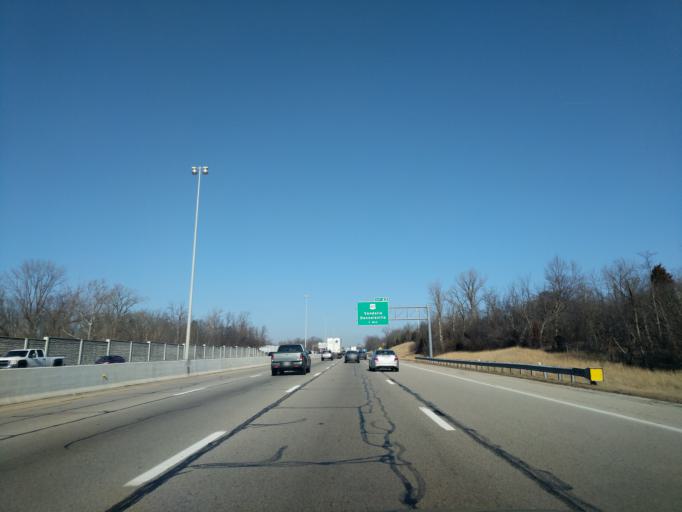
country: US
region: Ohio
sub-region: Montgomery County
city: Vandalia
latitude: 39.8728
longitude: -84.1881
